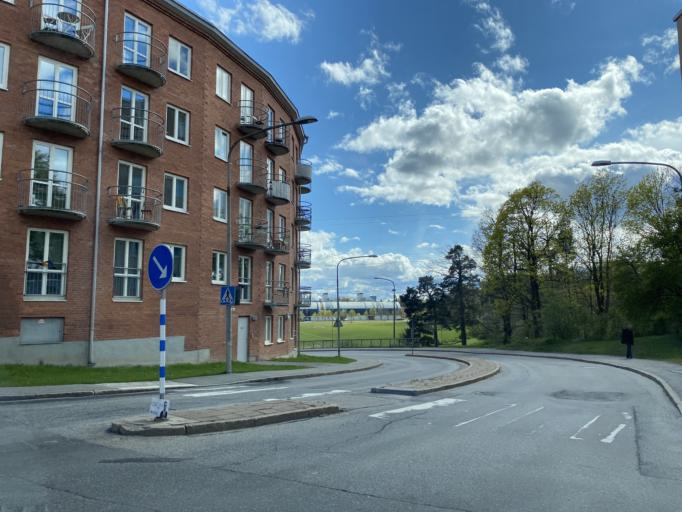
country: SE
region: Stockholm
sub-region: Norrtalje Kommun
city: Bergshamra
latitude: 59.3707
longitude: 18.0594
